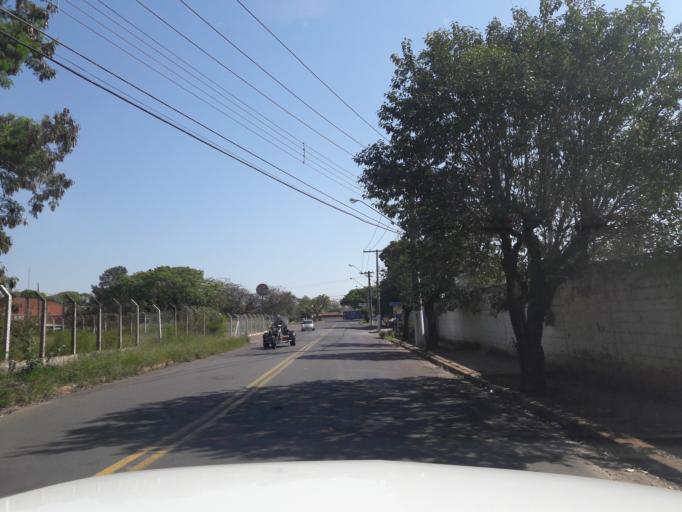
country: BR
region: Sao Paulo
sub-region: Moji-Guacu
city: Mogi-Gaucu
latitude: -22.3647
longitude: -46.9526
